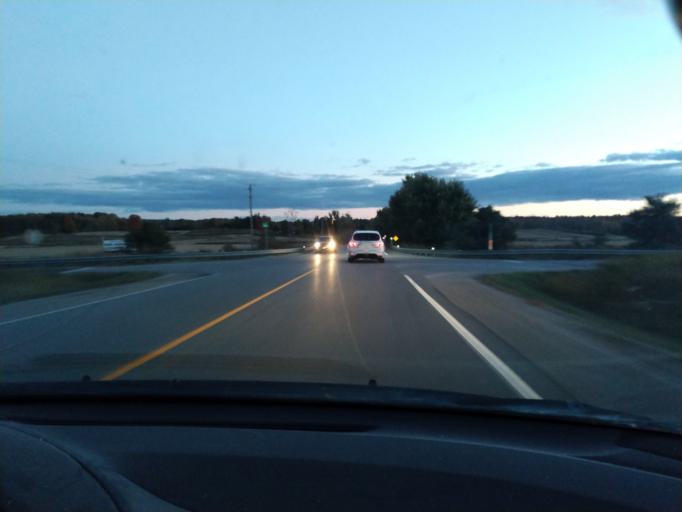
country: CA
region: Ontario
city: Bradford West Gwillimbury
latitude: 44.1714
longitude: -79.6573
